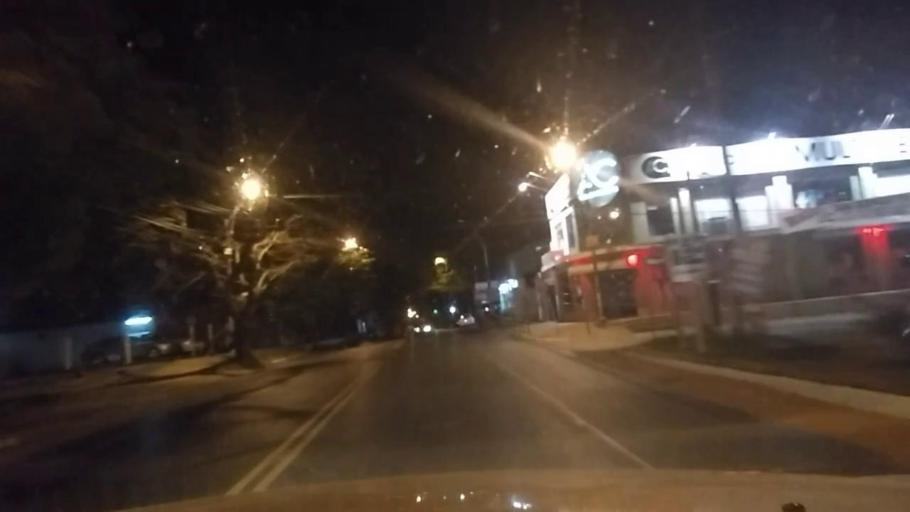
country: PY
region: Central
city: Ita
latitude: -25.5060
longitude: -57.3669
